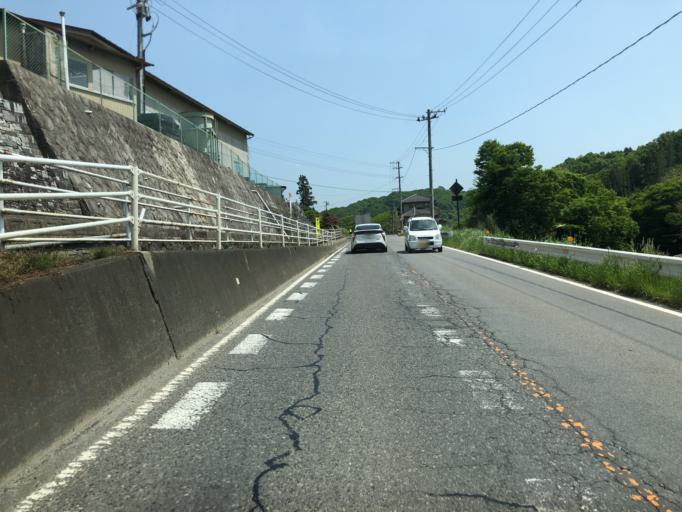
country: JP
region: Fukushima
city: Ishikawa
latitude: 37.1406
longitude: 140.4212
